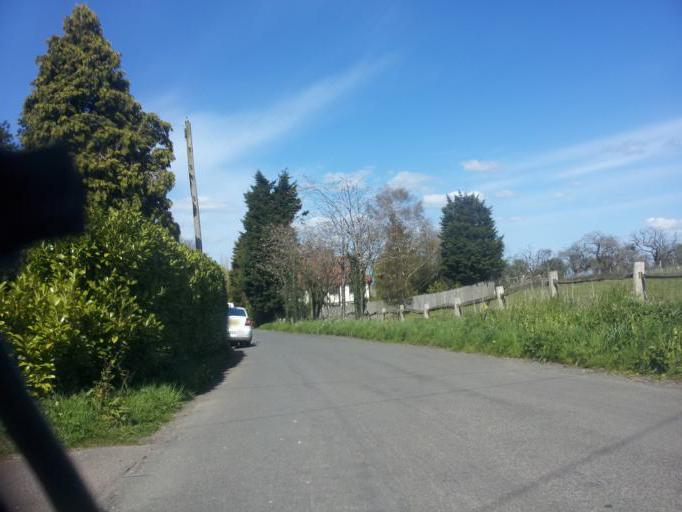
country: GB
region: England
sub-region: Kent
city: Newington
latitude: 51.3271
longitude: 0.6423
